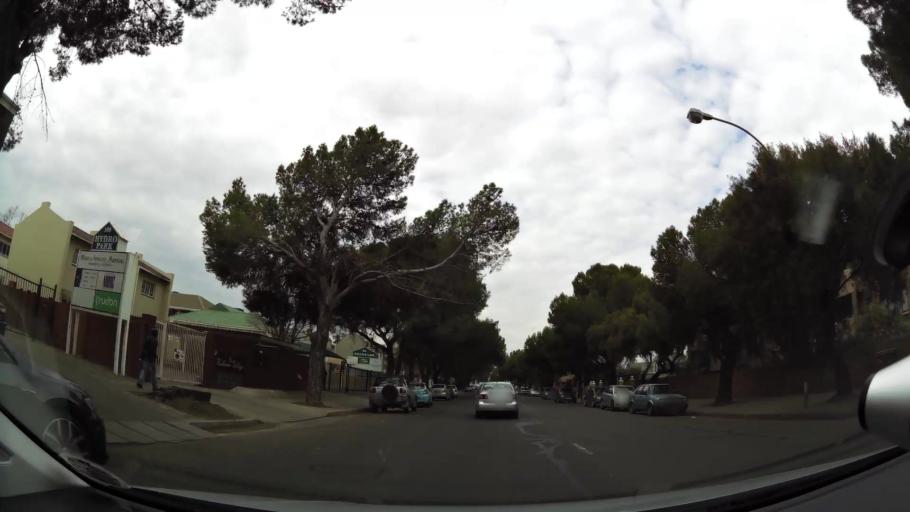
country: ZA
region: Orange Free State
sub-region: Mangaung Metropolitan Municipality
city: Bloemfontein
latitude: -29.1088
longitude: 26.2065
